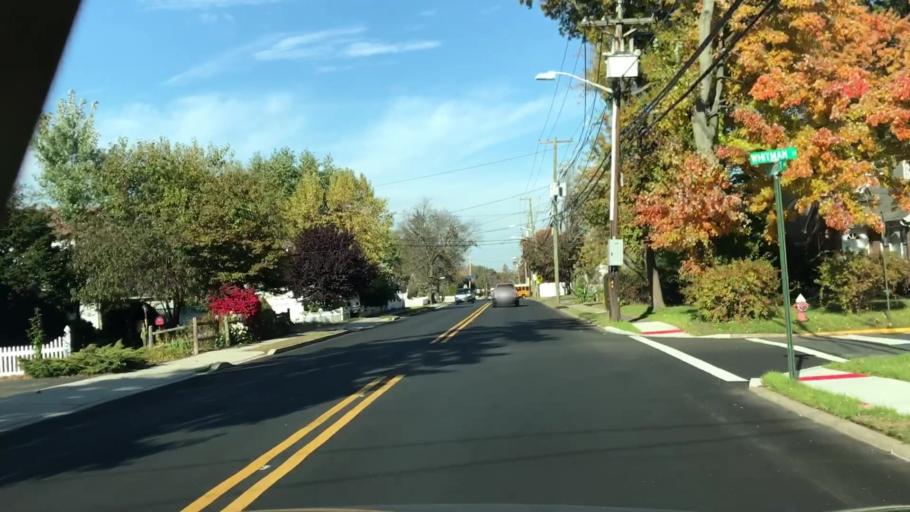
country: US
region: New Jersey
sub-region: Bergen County
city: Bergenfield
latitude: 40.9194
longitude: -74.0083
